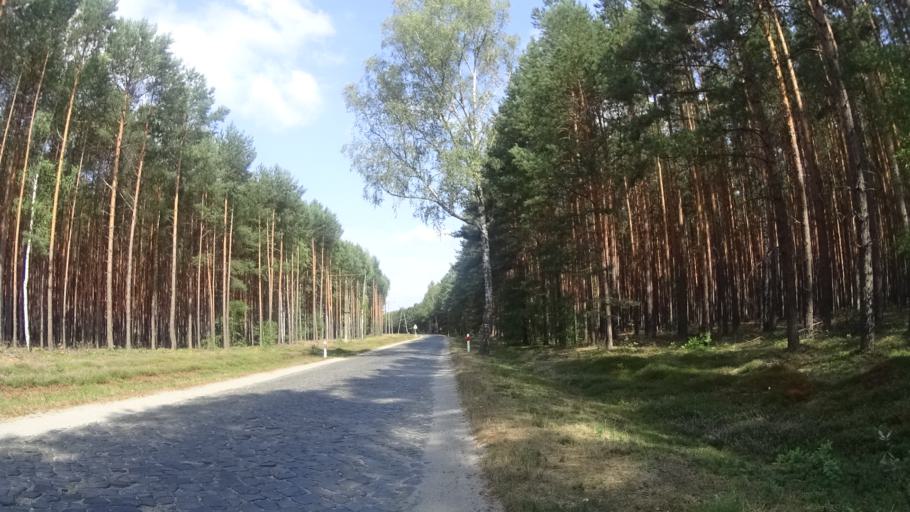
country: PL
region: Lubusz
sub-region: Powiat zarski
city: Leknica
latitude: 51.5095
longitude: 14.8365
